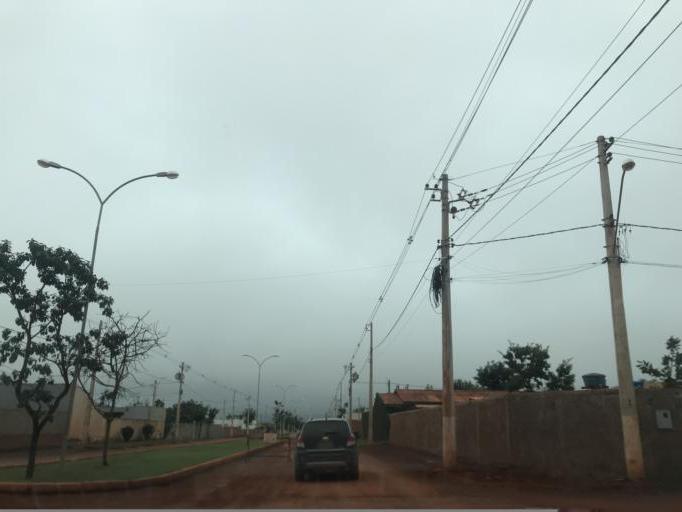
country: BR
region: Federal District
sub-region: Brasilia
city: Brasilia
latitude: -15.8281
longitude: -47.7951
